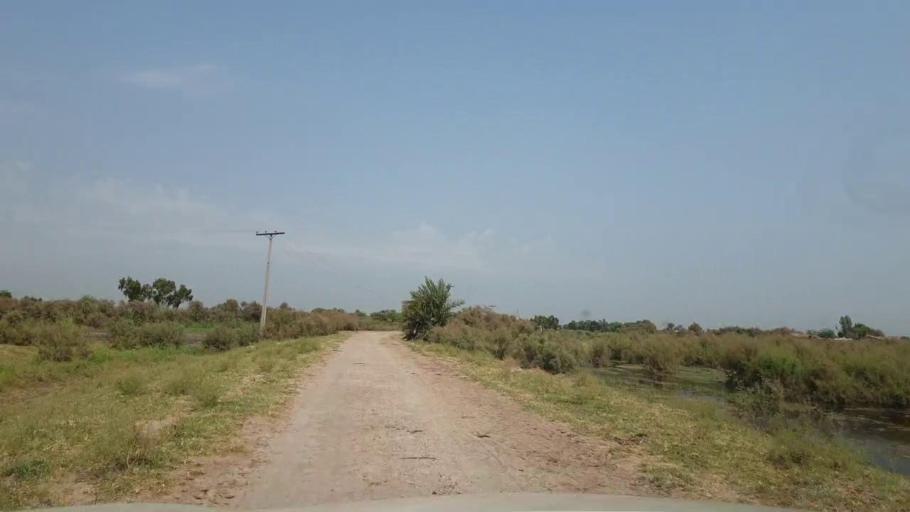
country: PK
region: Sindh
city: Ratodero
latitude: 27.8402
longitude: 68.2481
